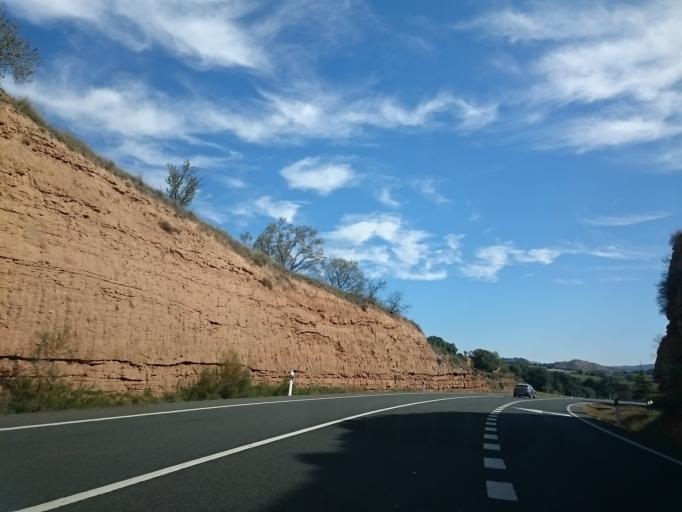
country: ES
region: Aragon
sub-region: Provincia de Huesca
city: Benavarri / Benabarre
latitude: 42.1086
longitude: 0.4866
